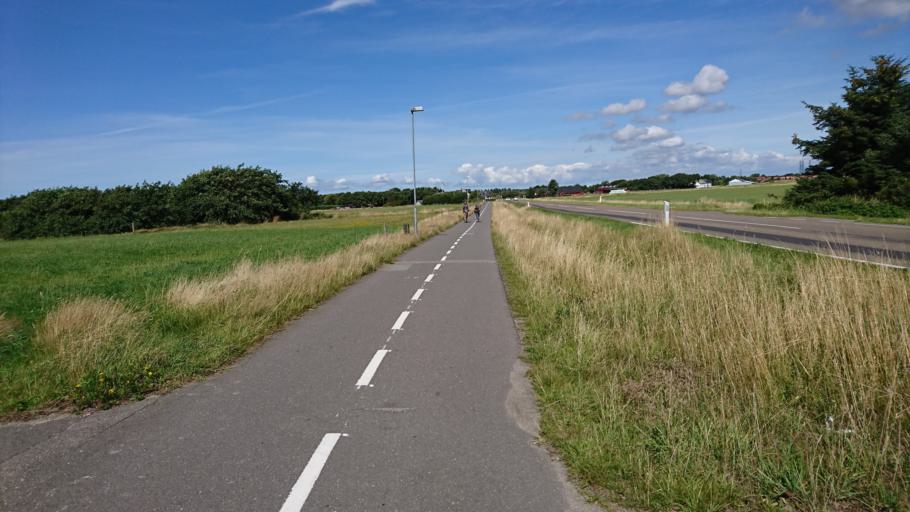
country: DK
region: South Denmark
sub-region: Fano Kommune
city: Nordby
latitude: 55.4285
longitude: 8.3956
